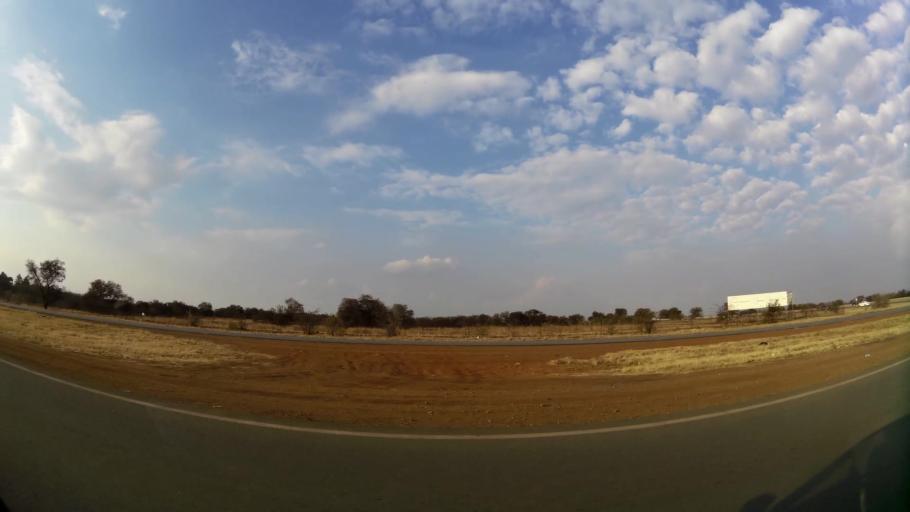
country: ZA
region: Gauteng
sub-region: Sedibeng District Municipality
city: Vereeniging
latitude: -26.6337
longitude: 27.8693
